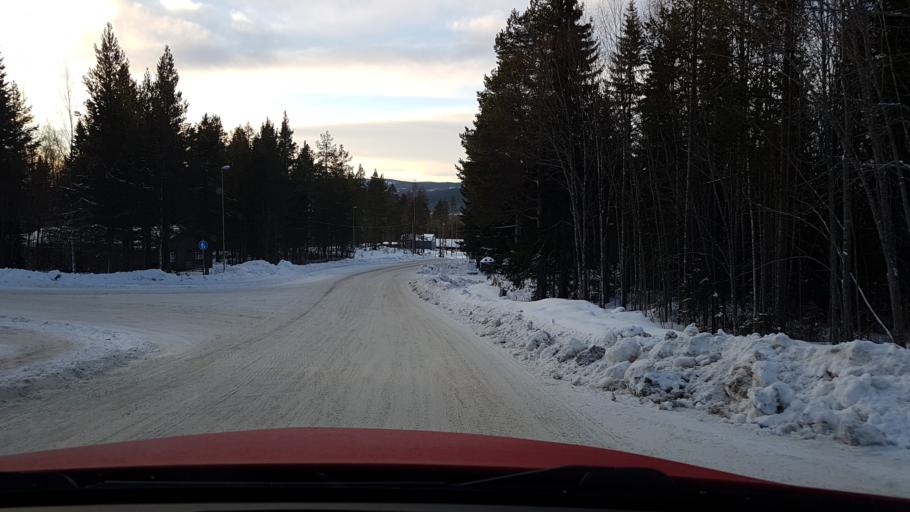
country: SE
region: Jaemtland
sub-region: Harjedalens Kommun
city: Sveg
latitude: 62.4174
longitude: 13.9459
